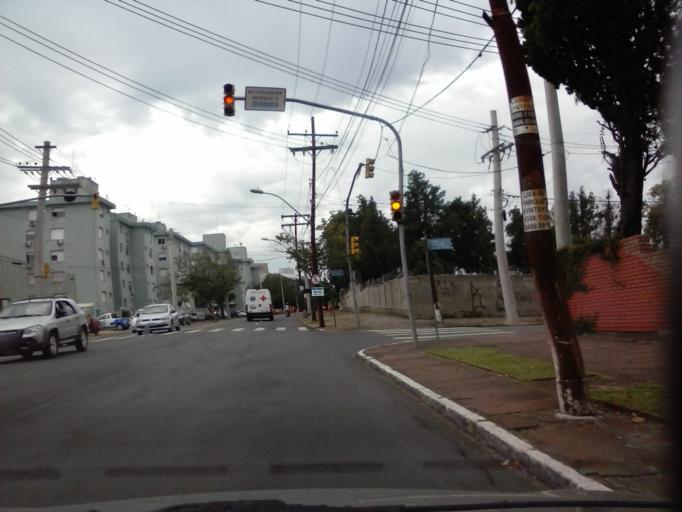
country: BR
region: Rio Grande do Sul
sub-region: Porto Alegre
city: Porto Alegre
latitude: -30.0588
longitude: -51.2085
